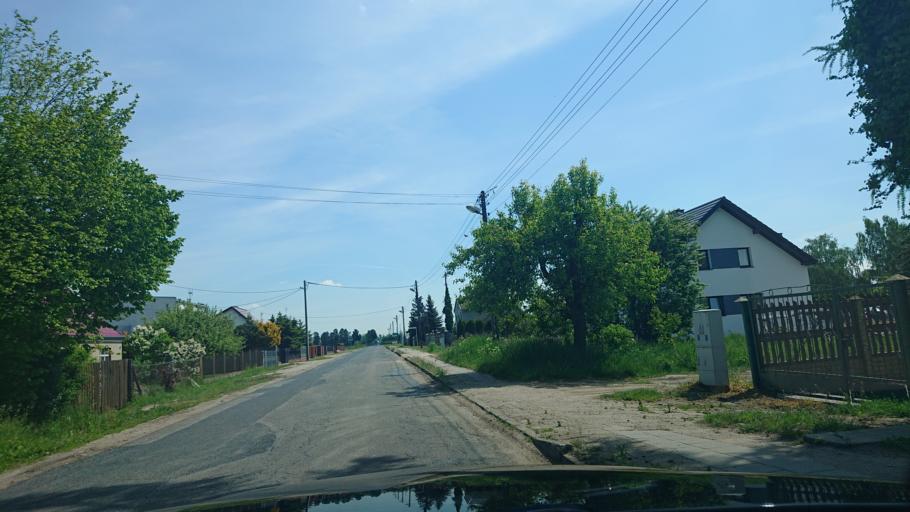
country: PL
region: Greater Poland Voivodeship
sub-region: Powiat gnieznienski
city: Niechanowo
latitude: 52.4543
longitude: 17.5973
